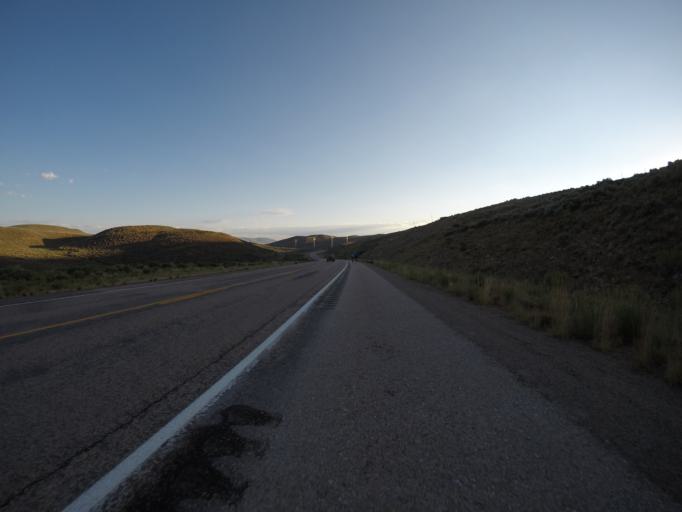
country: US
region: Wyoming
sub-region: Lincoln County
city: Kemmerer
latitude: 41.8629
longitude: -110.5274
